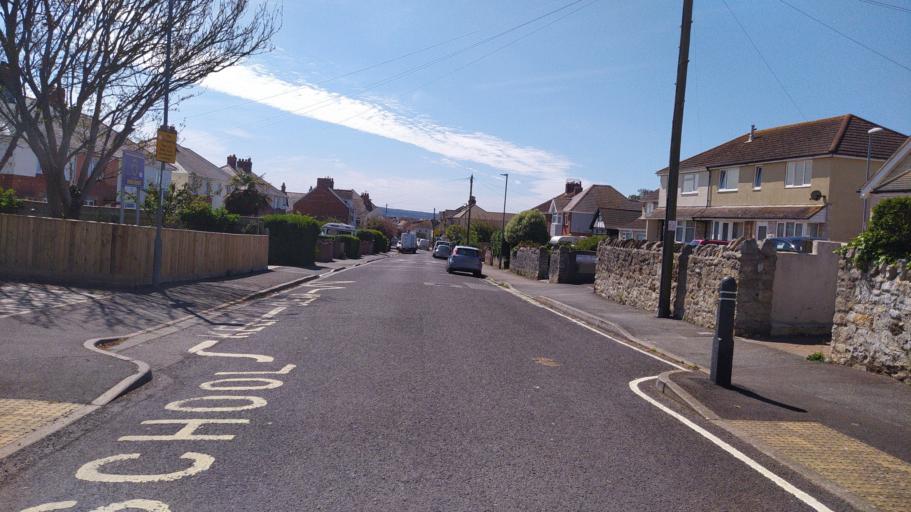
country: GB
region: England
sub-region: Dorset
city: Weymouth
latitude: 50.5942
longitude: -2.4783
